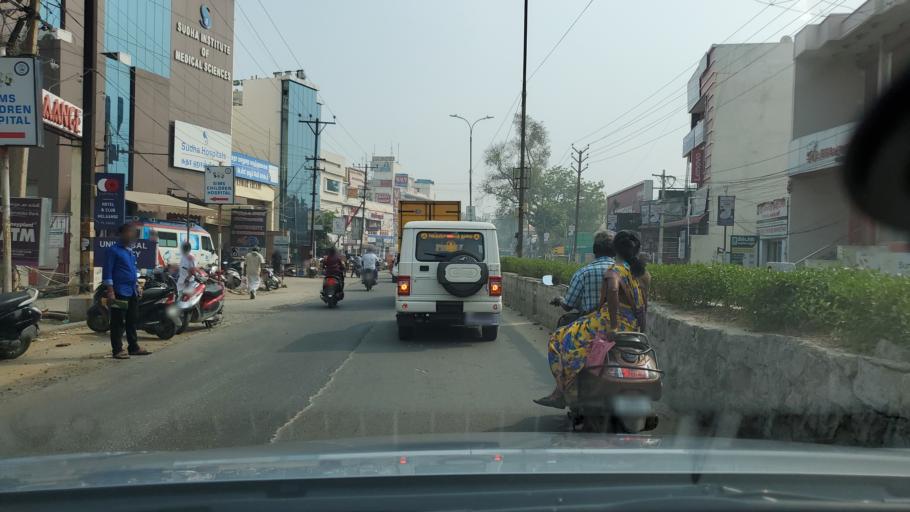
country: IN
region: Tamil Nadu
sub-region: Erode
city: Erode
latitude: 11.3367
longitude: 77.7108
